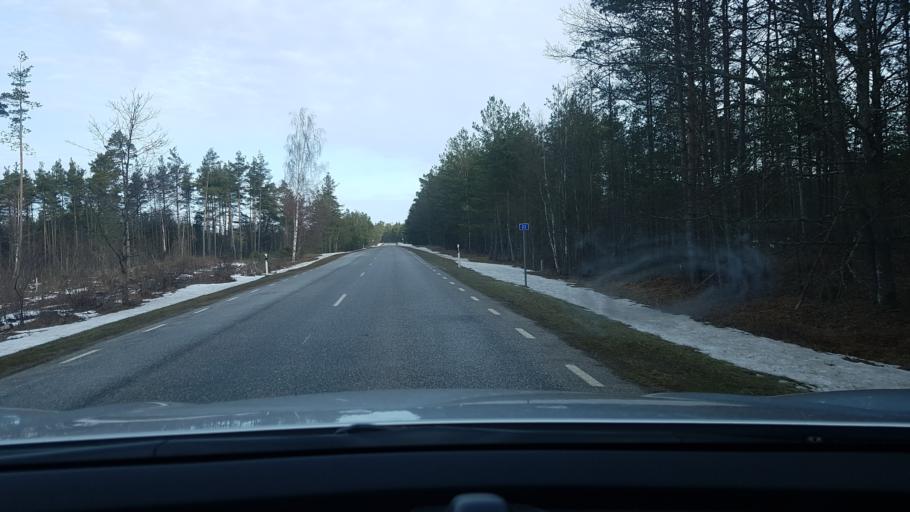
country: EE
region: Saare
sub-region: Kuressaare linn
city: Kuressaare
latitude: 58.4419
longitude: 22.7055
